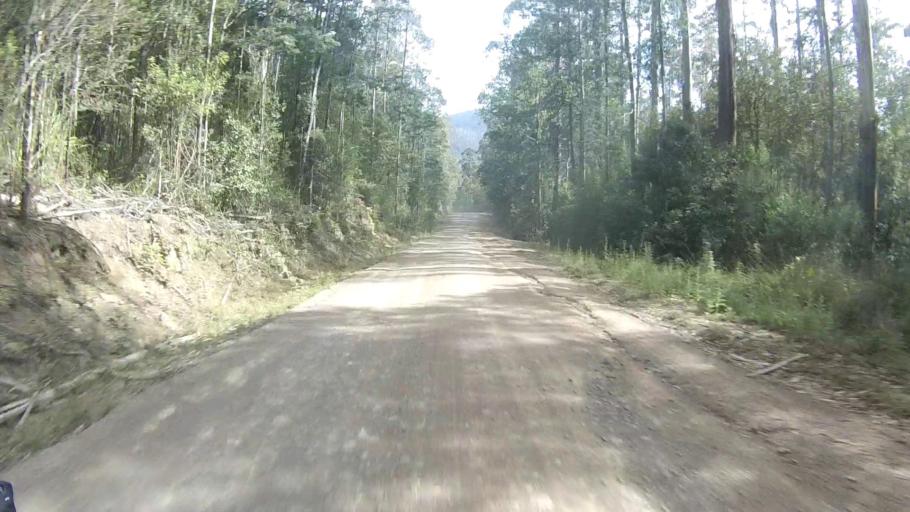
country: AU
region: Tasmania
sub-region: Sorell
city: Sorell
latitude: -42.7148
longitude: 147.8410
